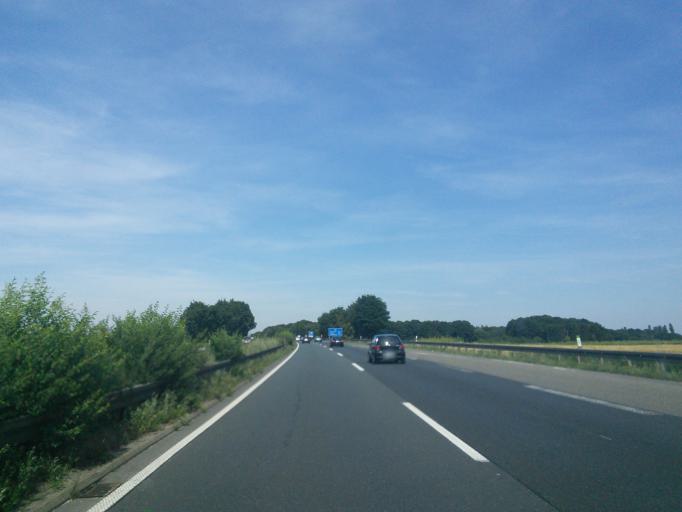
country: DE
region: North Rhine-Westphalia
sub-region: Regierungsbezirk Dusseldorf
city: Viersen
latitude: 51.2128
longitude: 6.3894
